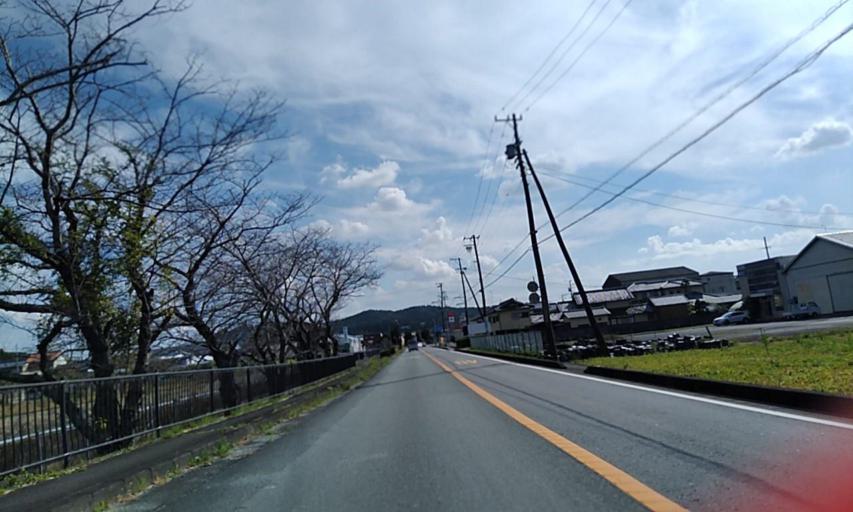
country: JP
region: Shizuoka
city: Hamakita
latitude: 34.8391
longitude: 137.8396
